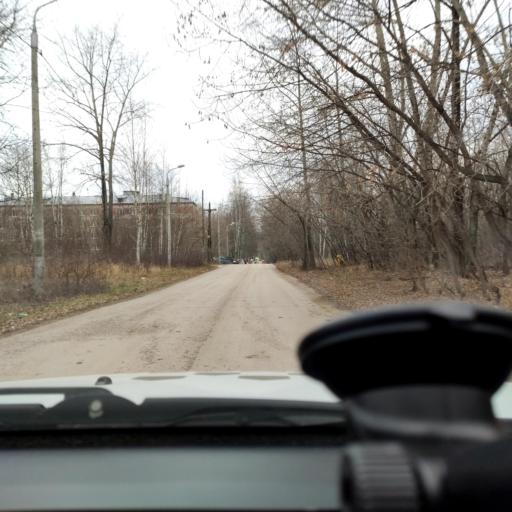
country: RU
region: Perm
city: Perm
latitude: 58.1182
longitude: 56.3749
